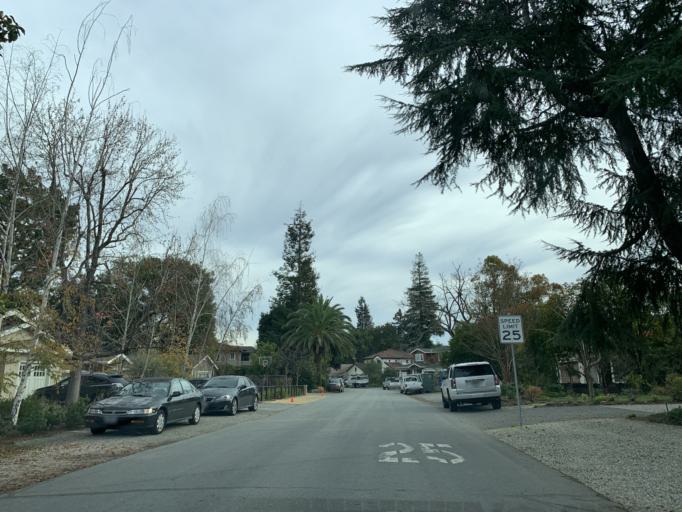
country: US
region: California
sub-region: Santa Clara County
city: Los Altos
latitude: 37.3769
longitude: -122.1042
